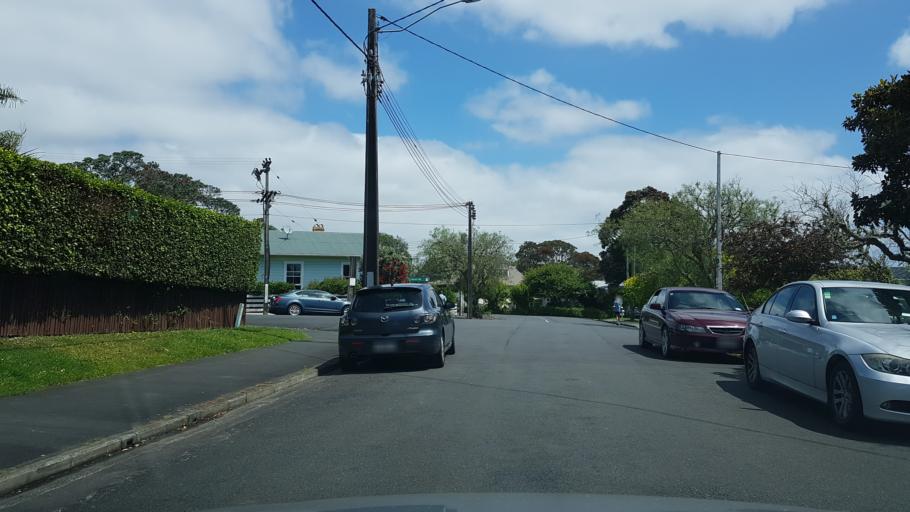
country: NZ
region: Auckland
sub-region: Auckland
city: North Shore
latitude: -36.8161
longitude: 174.7430
